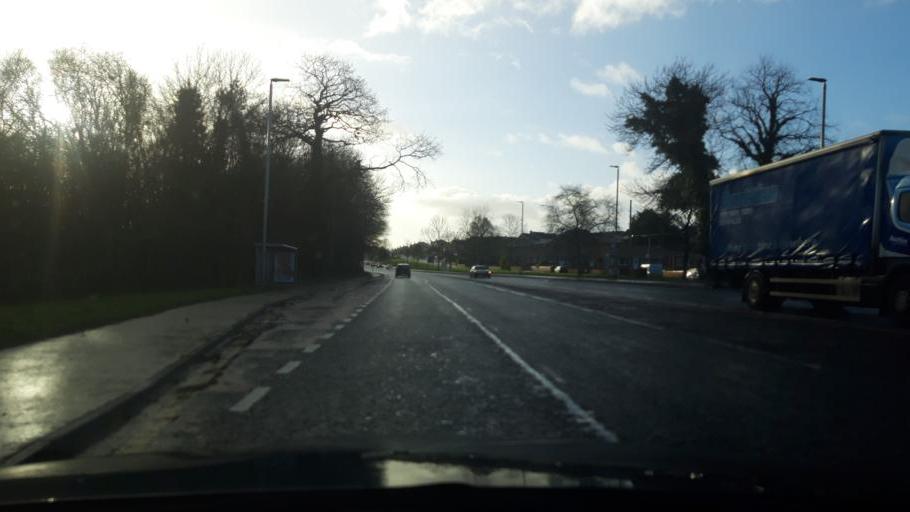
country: GB
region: Northern Ireland
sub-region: Coleraine District
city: Coleraine
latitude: 55.1193
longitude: -6.6811
